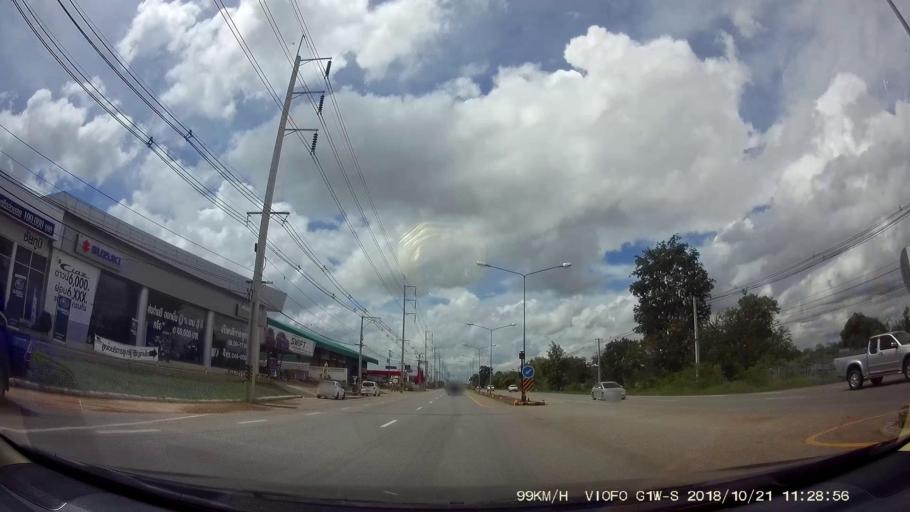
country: TH
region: Chaiyaphum
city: Chaiyaphum
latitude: 15.7881
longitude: 102.0375
